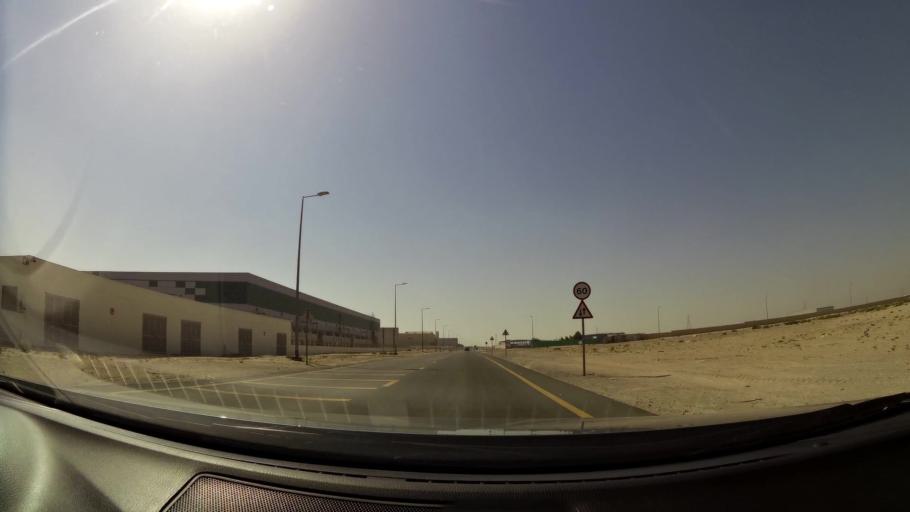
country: AE
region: Dubai
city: Dubai
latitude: 24.9167
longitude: 55.0660
